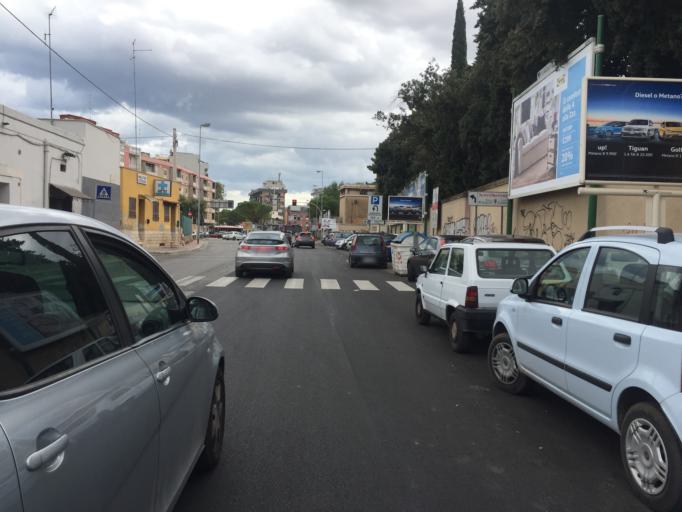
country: IT
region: Apulia
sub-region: Provincia di Bari
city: Bari
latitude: 41.1075
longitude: 16.8575
